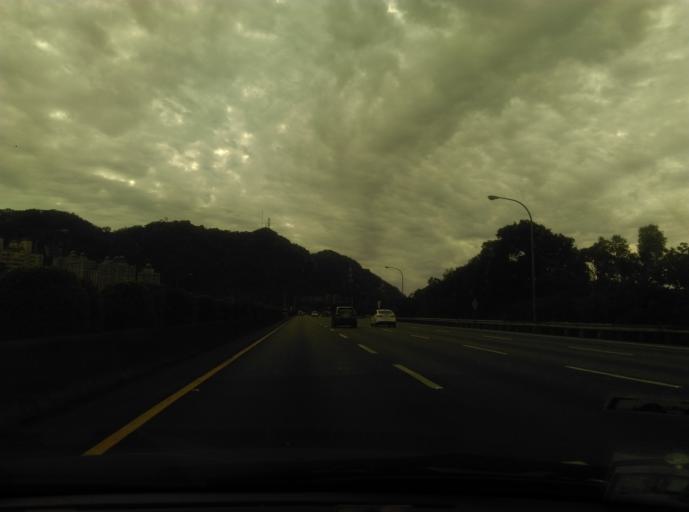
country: TW
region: Taiwan
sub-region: Taoyuan
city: Taoyuan
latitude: 24.9424
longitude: 121.3637
